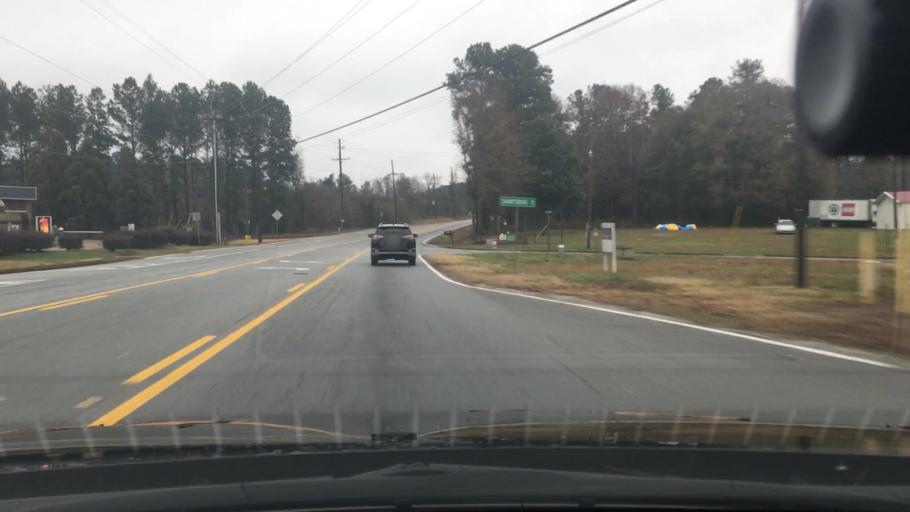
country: US
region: Georgia
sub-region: Fayette County
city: Peachtree City
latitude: 33.4071
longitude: -84.6823
